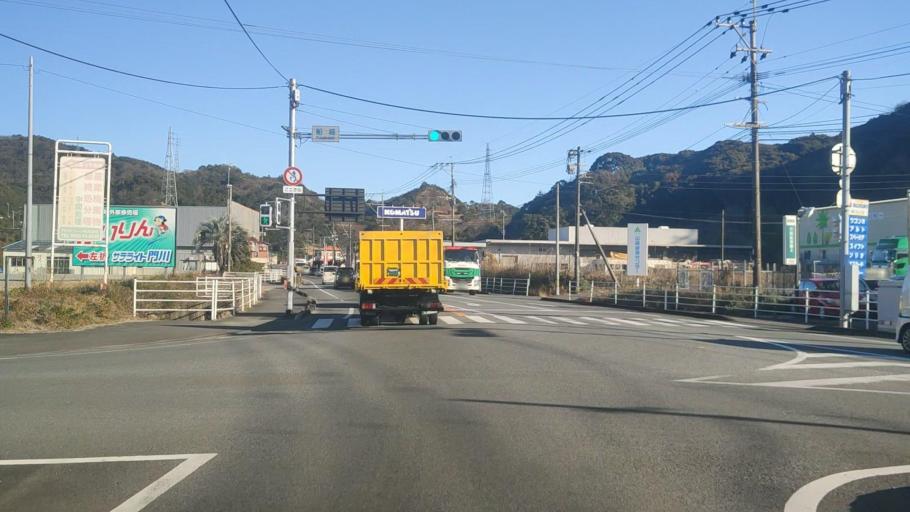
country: JP
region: Miyazaki
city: Nobeoka
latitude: 32.4982
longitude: 131.6626
